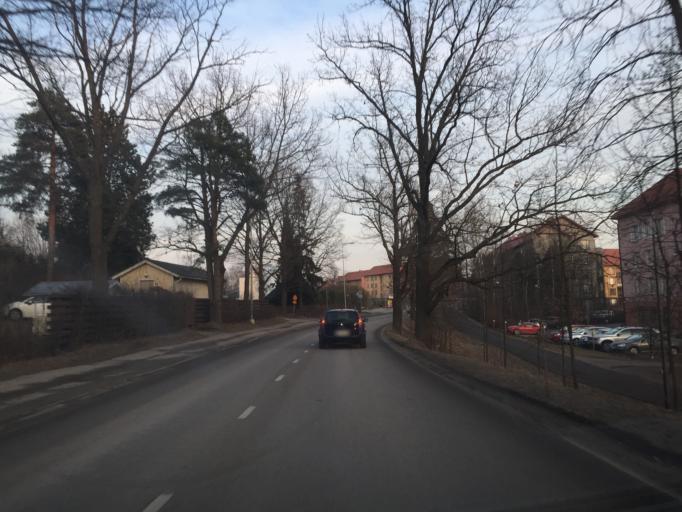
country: FI
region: Uusimaa
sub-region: Helsinki
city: Vantaa
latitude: 60.2852
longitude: 24.9628
